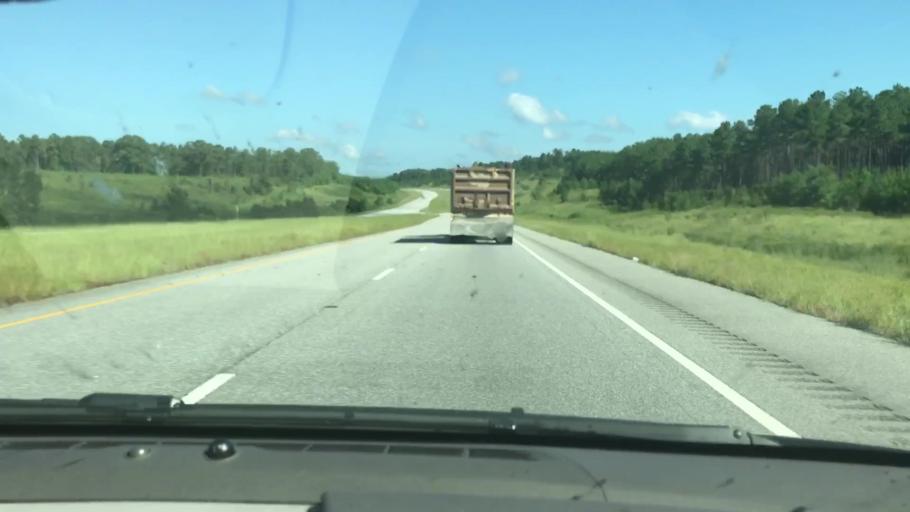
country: US
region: Alabama
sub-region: Barbour County
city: Eufaula
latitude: 32.1240
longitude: -85.1528
